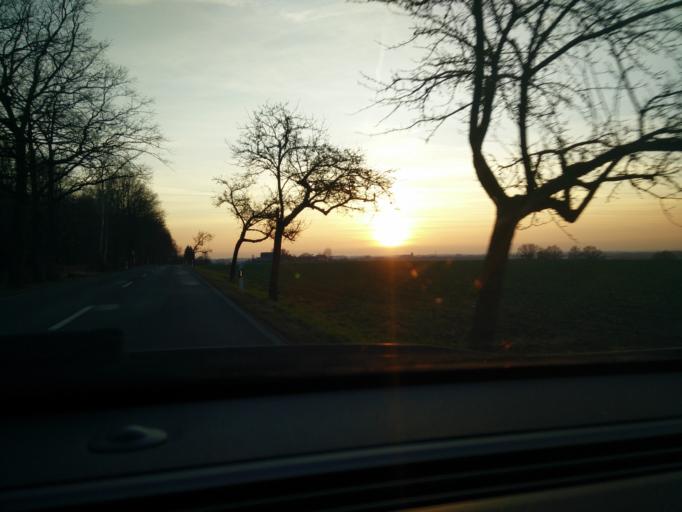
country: DE
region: Saxony
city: Geithain
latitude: 51.0731
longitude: 12.7205
